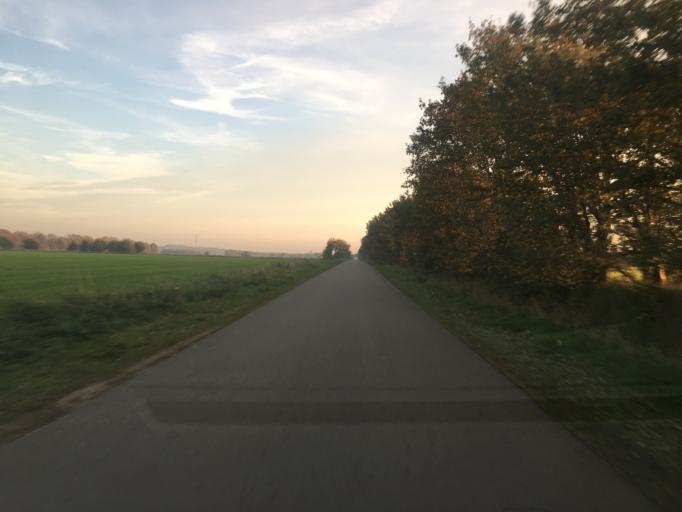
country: DK
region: South Denmark
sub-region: Tonder Kommune
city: Toftlund
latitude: 55.0482
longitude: 9.1092
